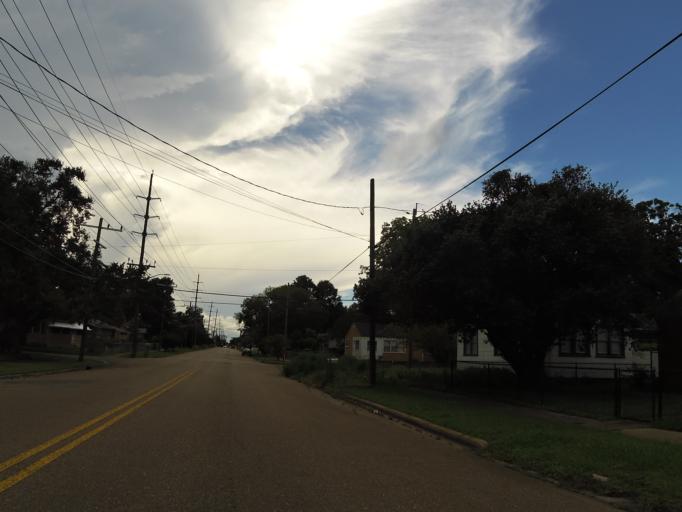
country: US
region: Florida
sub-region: Duval County
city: Jacksonville
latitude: 30.3727
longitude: -81.6479
